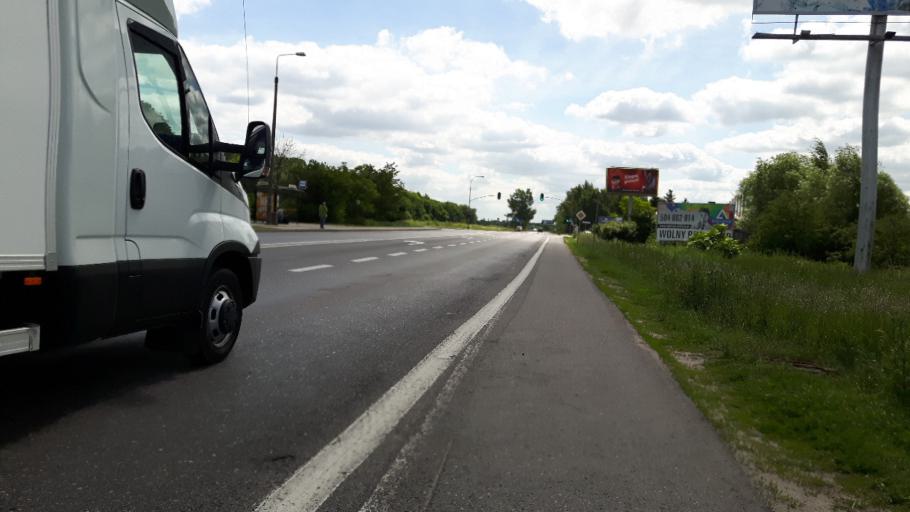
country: PL
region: Pomeranian Voivodeship
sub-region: Gdansk
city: Gdansk
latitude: 54.3442
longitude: 18.7212
